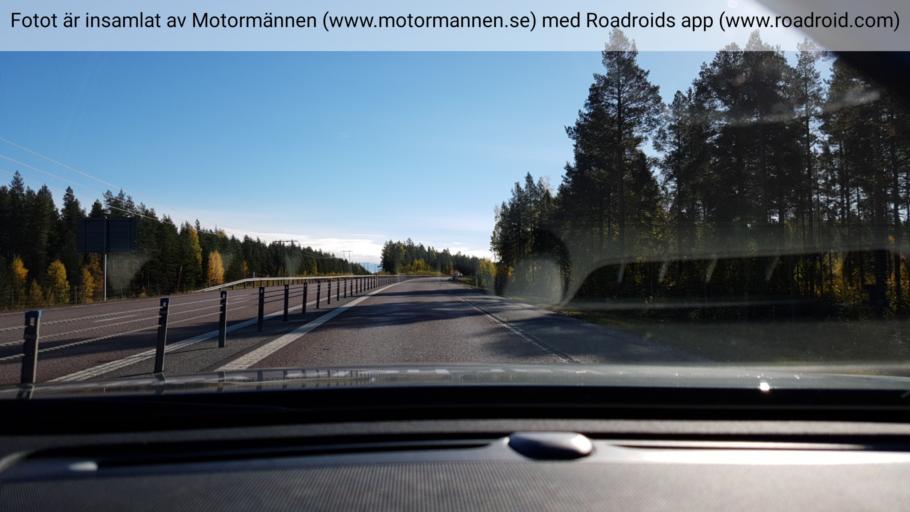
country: SE
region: Vaesterbotten
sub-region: Skelleftea Kommun
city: Burea
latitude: 64.6425
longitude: 21.1562
